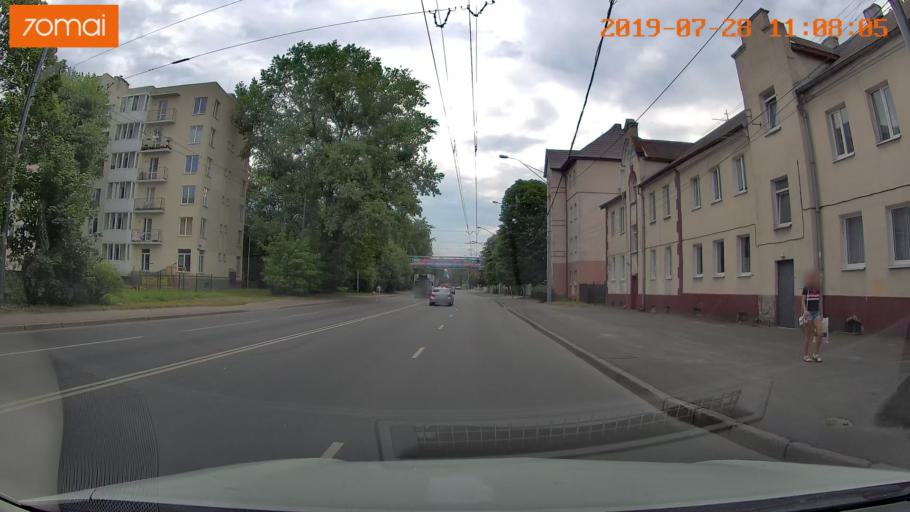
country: RU
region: Kaliningrad
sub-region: Gorod Kaliningrad
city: Kaliningrad
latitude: 54.7113
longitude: 20.4379
